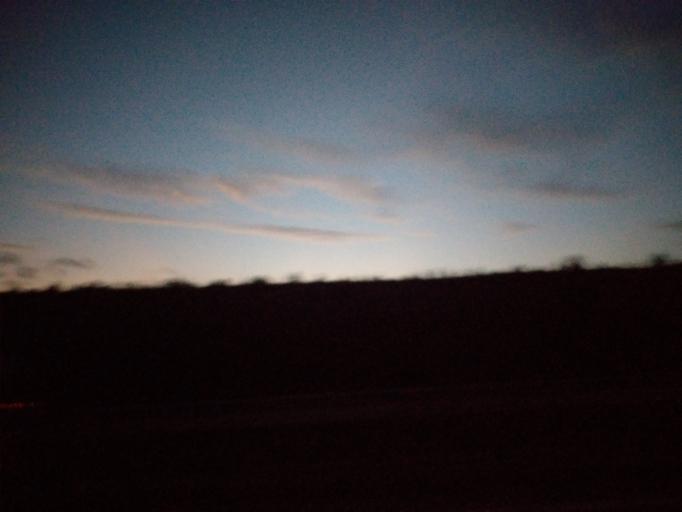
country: TR
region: Ankara
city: Kazan
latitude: 40.1570
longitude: 32.5962
